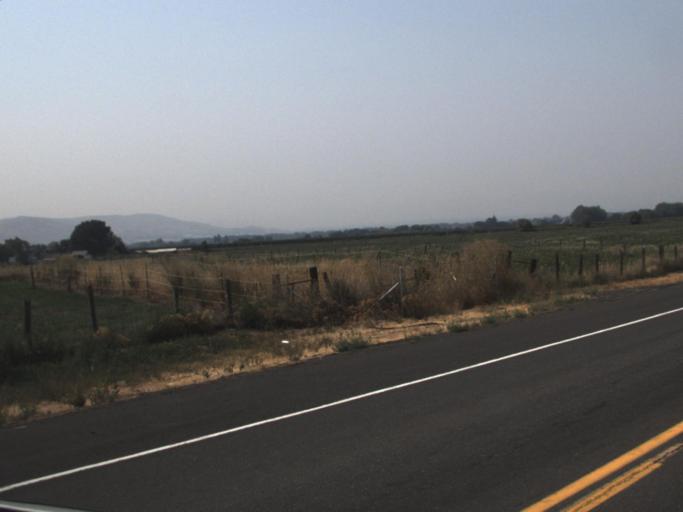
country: US
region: Washington
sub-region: Yakima County
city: Terrace Heights
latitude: 46.5647
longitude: -120.4100
